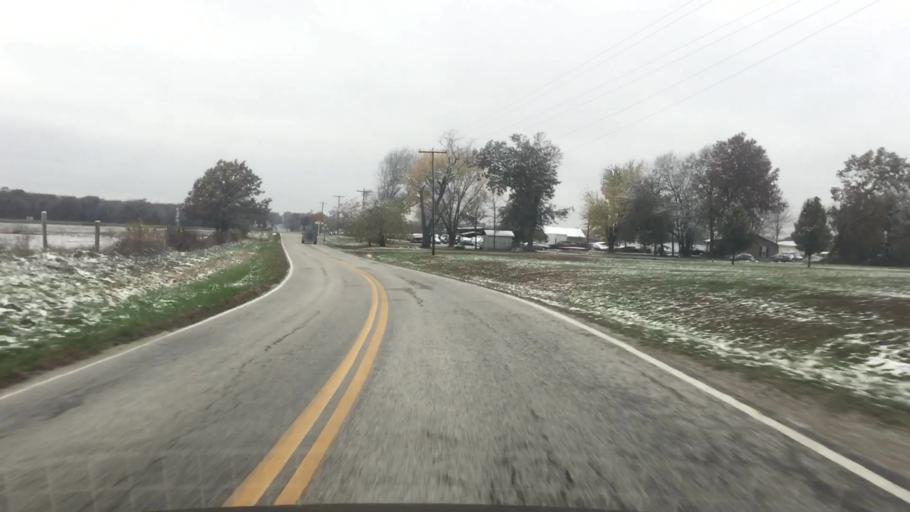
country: US
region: Missouri
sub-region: Saint Clair County
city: Osceola
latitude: 37.9899
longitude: -93.6470
